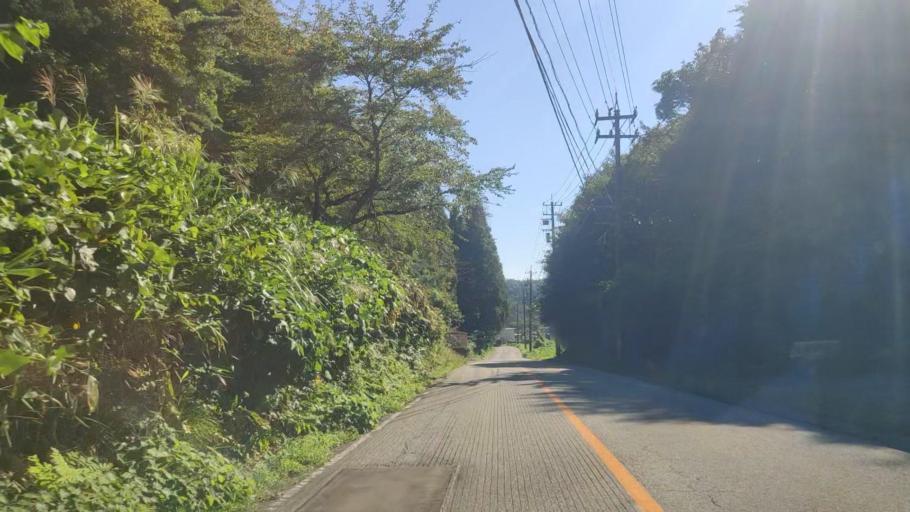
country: JP
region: Ishikawa
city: Nanao
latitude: 37.3200
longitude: 137.1660
